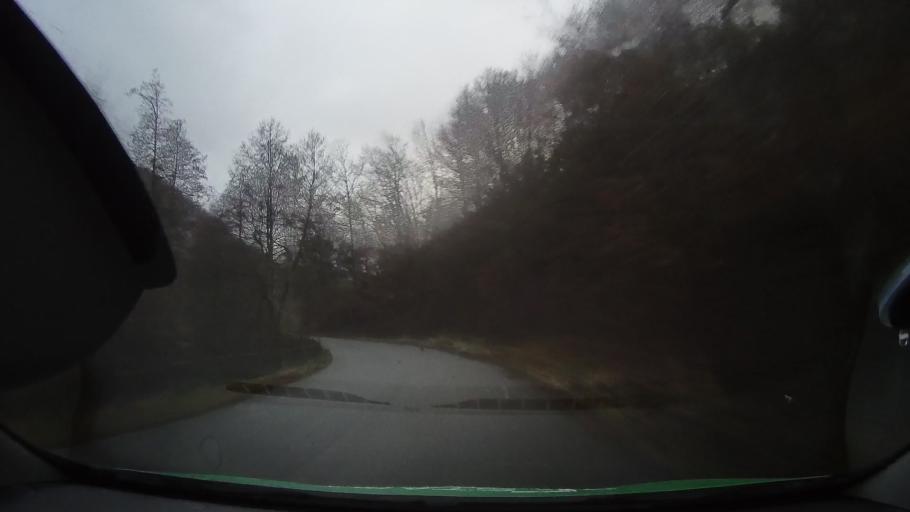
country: RO
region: Hunedoara
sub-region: Comuna Ribita
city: Ribita
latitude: 46.2713
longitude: 22.7424
